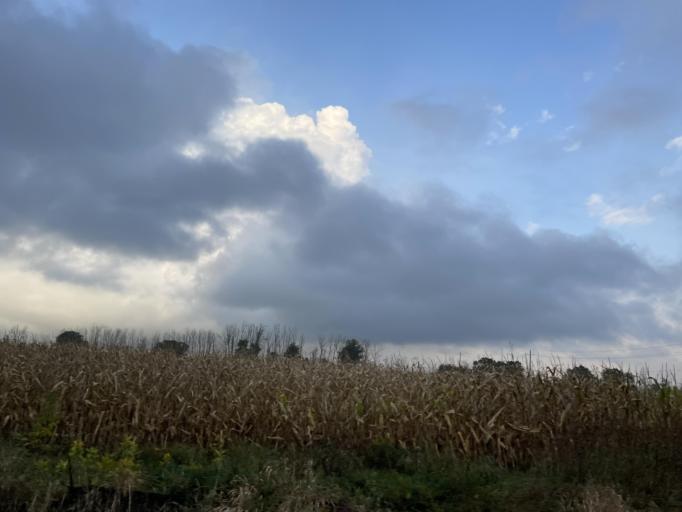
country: CA
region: Ontario
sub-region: Wellington County
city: Guelph
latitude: 43.5083
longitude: -80.2728
